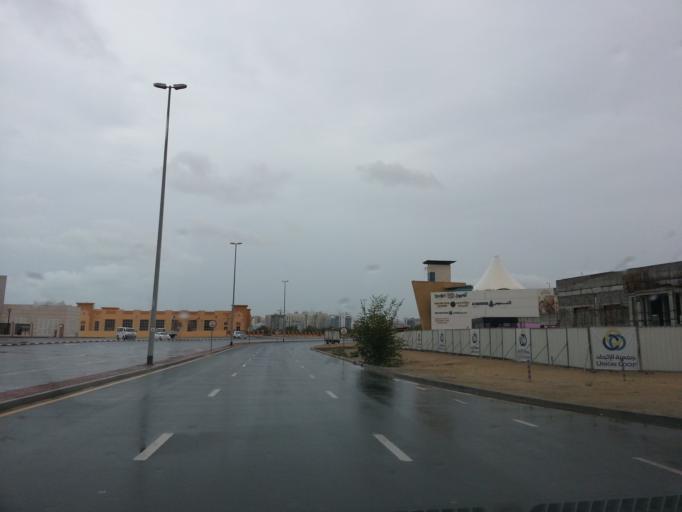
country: AE
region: Dubai
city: Dubai
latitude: 25.0972
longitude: 55.2032
